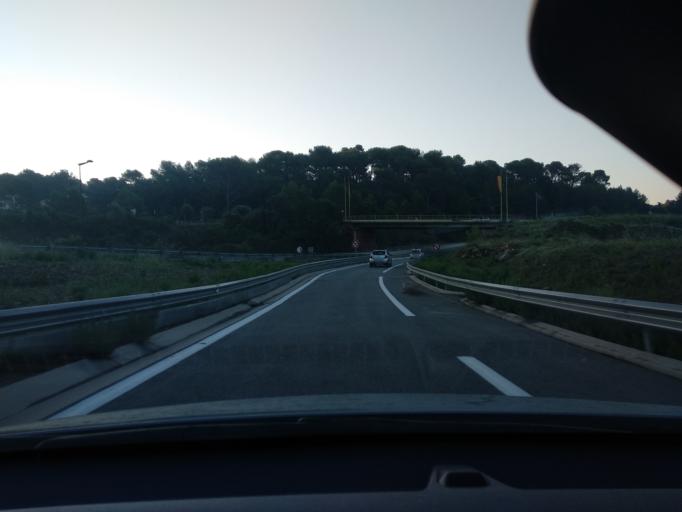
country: FR
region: Provence-Alpes-Cote d'Azur
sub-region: Departement des Alpes-Maritimes
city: Grasse
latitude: 43.6418
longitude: 6.9346
